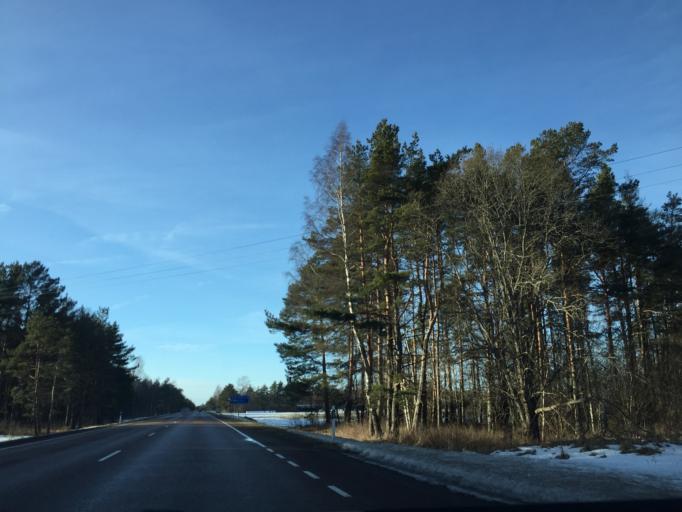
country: EE
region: Saare
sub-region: Orissaare vald
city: Orissaare
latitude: 58.5297
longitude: 22.9992
